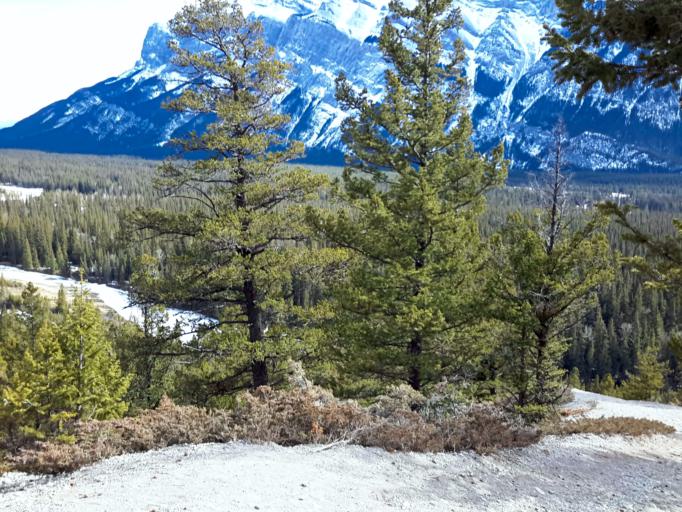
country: CA
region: Alberta
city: Banff
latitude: 51.1888
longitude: -115.5300
